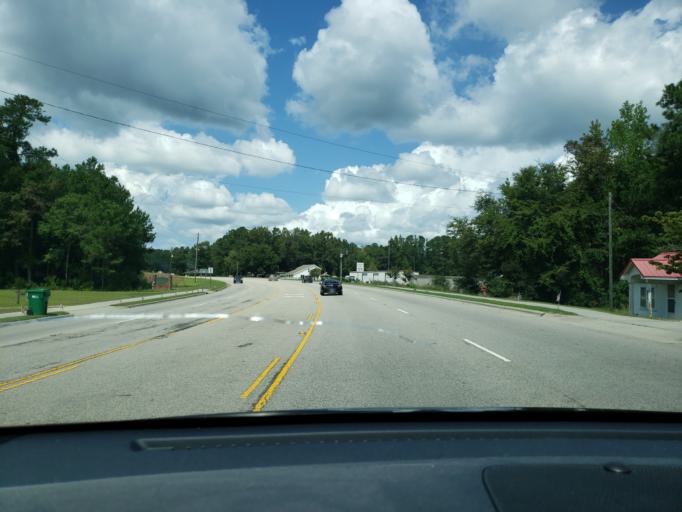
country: US
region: North Carolina
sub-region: Bladen County
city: Elizabethtown
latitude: 34.6628
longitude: -78.7270
